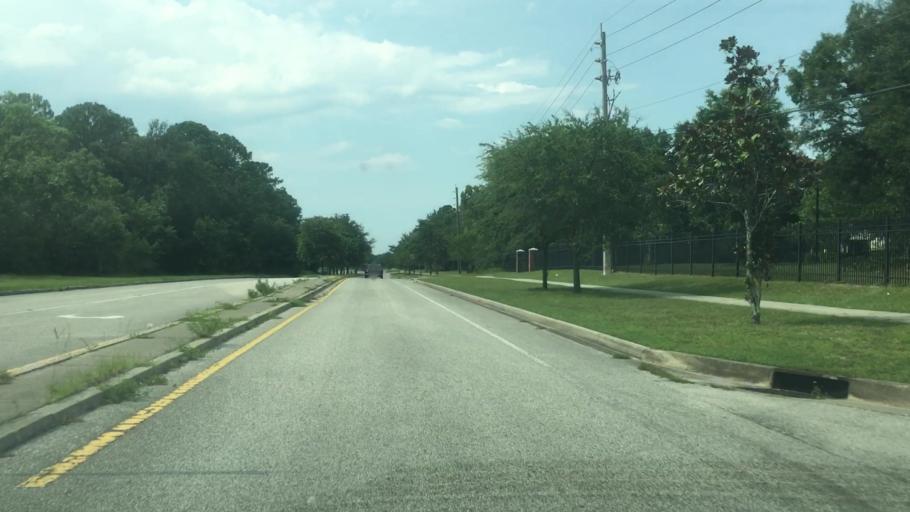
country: US
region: Florida
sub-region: Duval County
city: Neptune Beach
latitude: 30.2968
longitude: -81.5050
